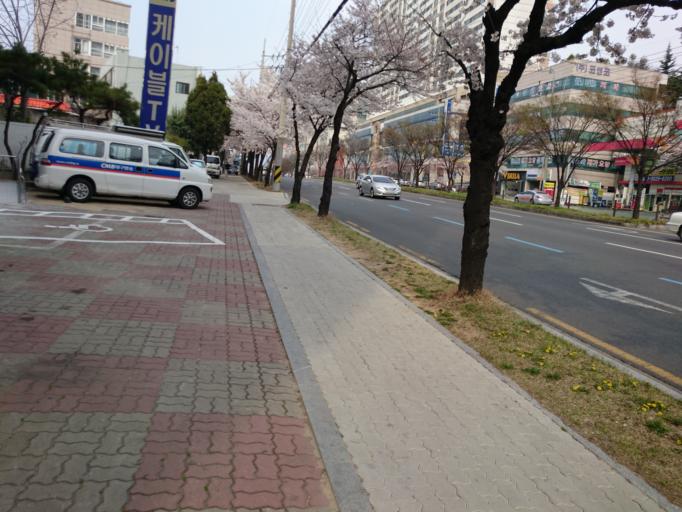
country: KR
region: Daegu
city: Daegu
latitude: 35.8681
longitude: 128.6307
